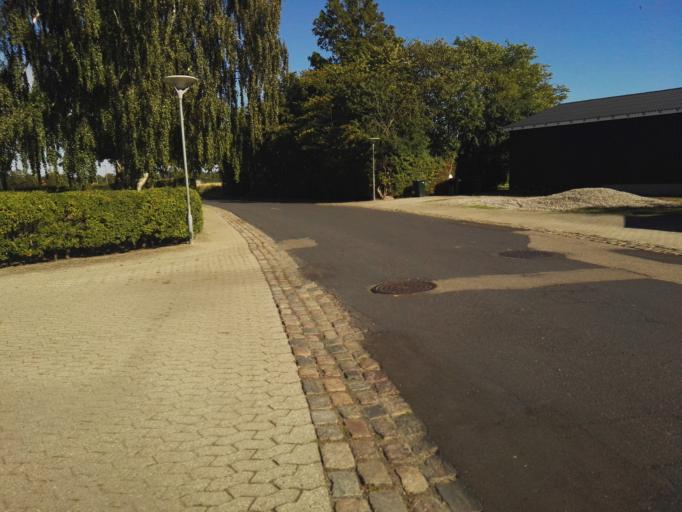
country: DK
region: Zealand
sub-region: Odsherred Kommune
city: Nykobing Sjaelland
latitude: 55.9264
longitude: 11.6831
